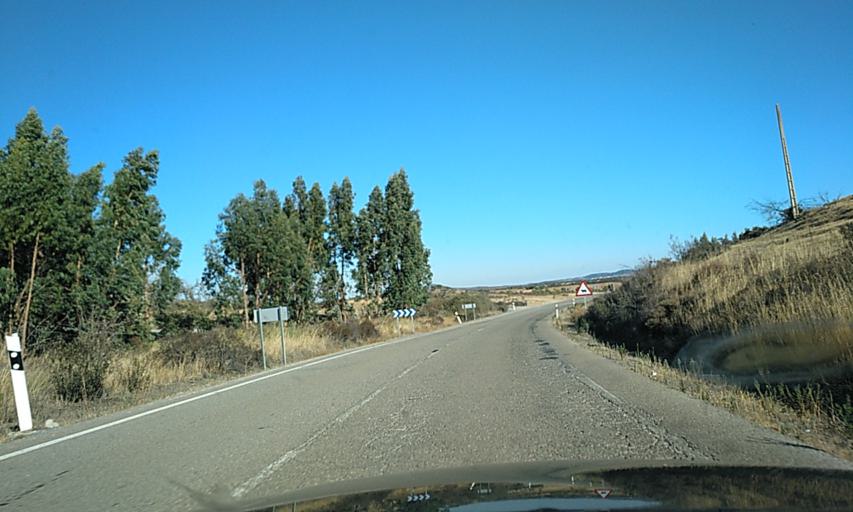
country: ES
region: Andalusia
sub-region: Provincia de Huelva
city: Santa Barbara de Casa
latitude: 37.7880
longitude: -7.1681
